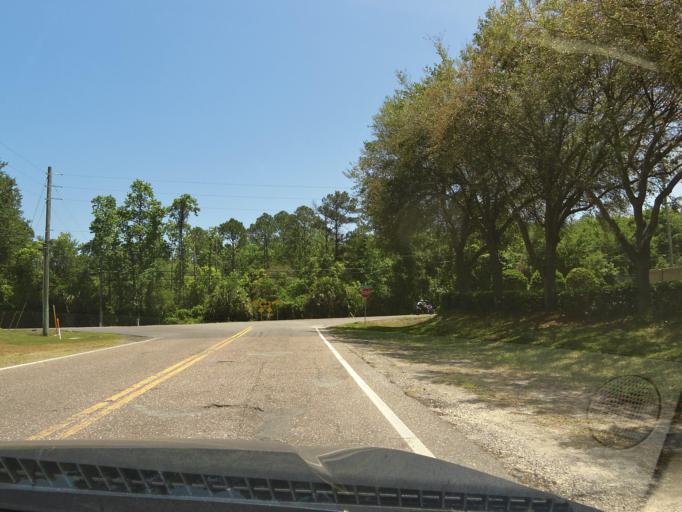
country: US
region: Florida
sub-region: Duval County
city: Jacksonville
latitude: 30.4216
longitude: -81.5657
